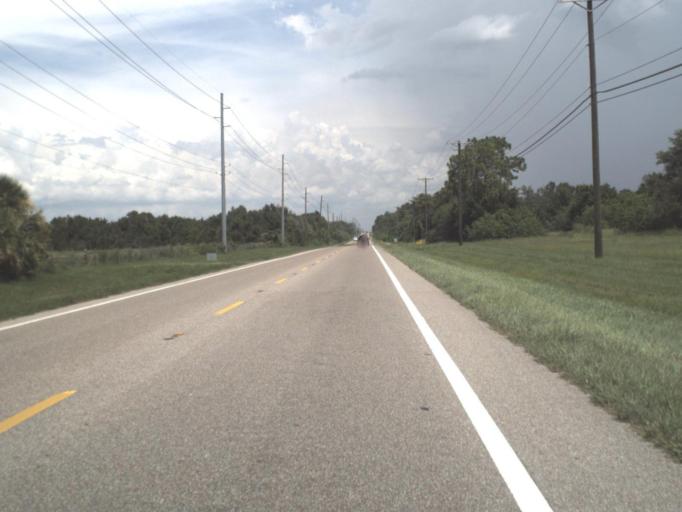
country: US
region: Florida
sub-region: Hillsborough County
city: Sun City Center
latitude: 27.7455
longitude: -82.3352
